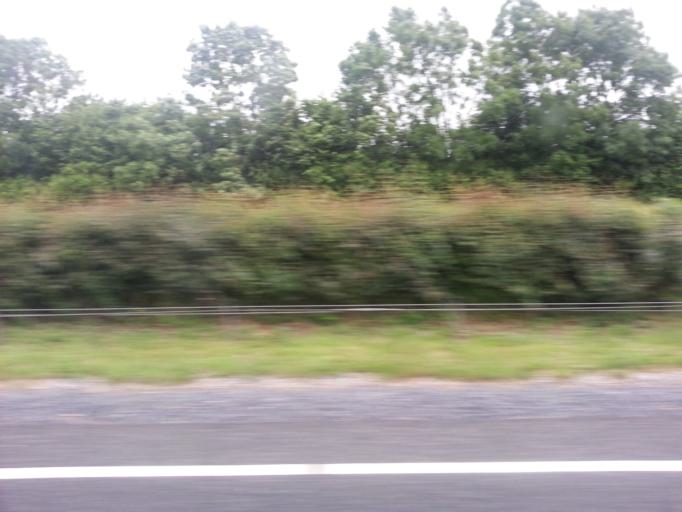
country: IE
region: Leinster
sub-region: Kildare
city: Kilcullen
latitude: 53.1304
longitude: -6.7645
